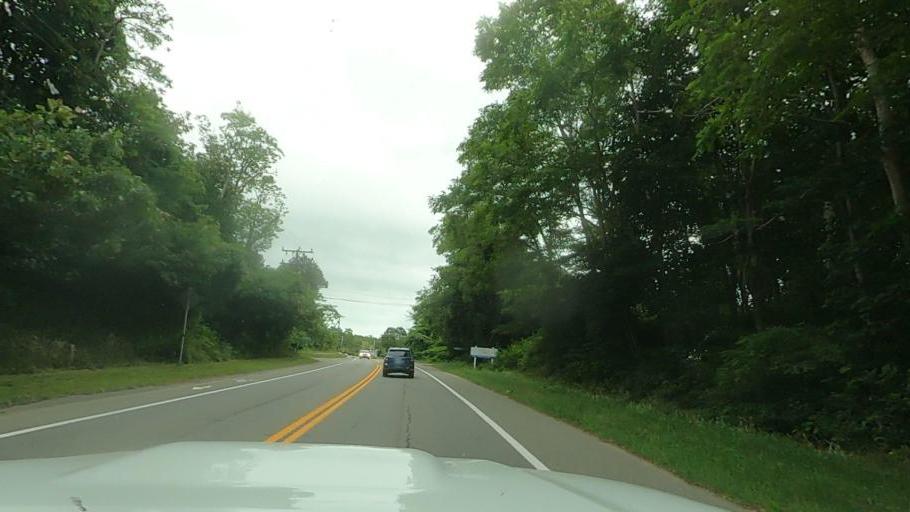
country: US
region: Massachusetts
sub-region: Barnstable County
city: Wellfleet
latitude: 41.9502
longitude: -70.0333
